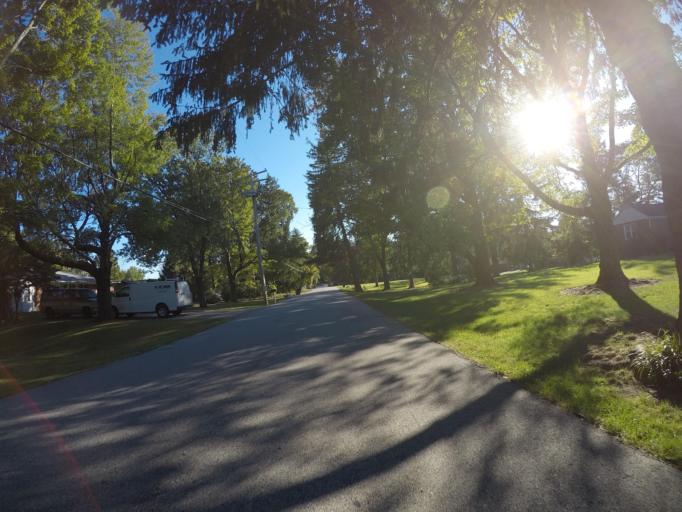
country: US
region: Maryland
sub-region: Howard County
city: Ellicott City
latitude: 39.2939
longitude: -76.8032
